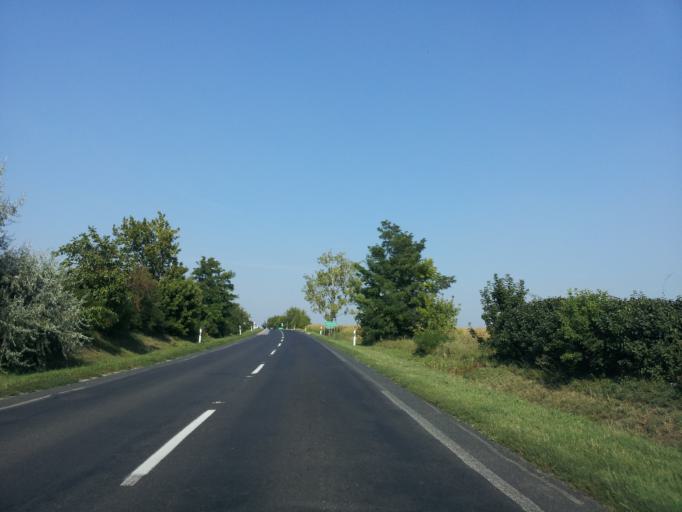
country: HU
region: Somogy
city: Balatonszabadi
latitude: 46.9478
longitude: 18.1771
